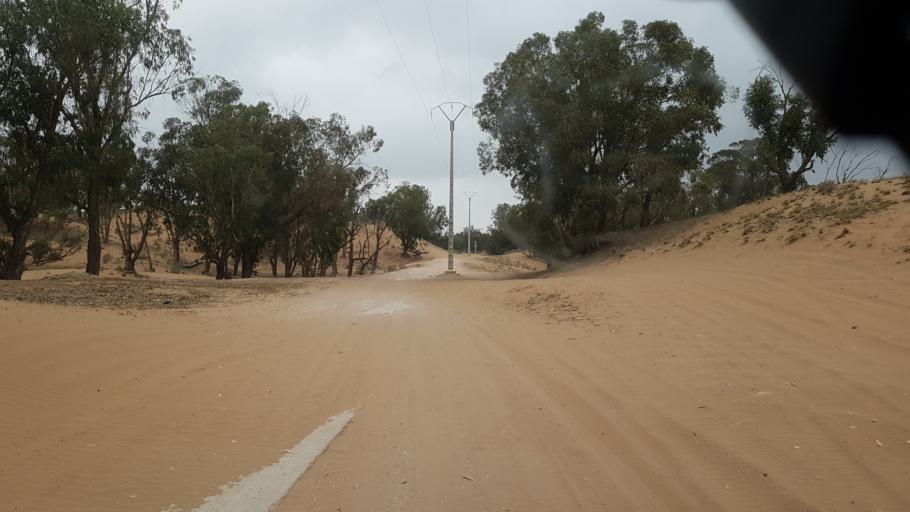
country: MA
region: Souss-Massa-Draa
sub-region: Inezgane-Ait Mellou
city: Inezgane
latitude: 30.3159
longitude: -9.5382
